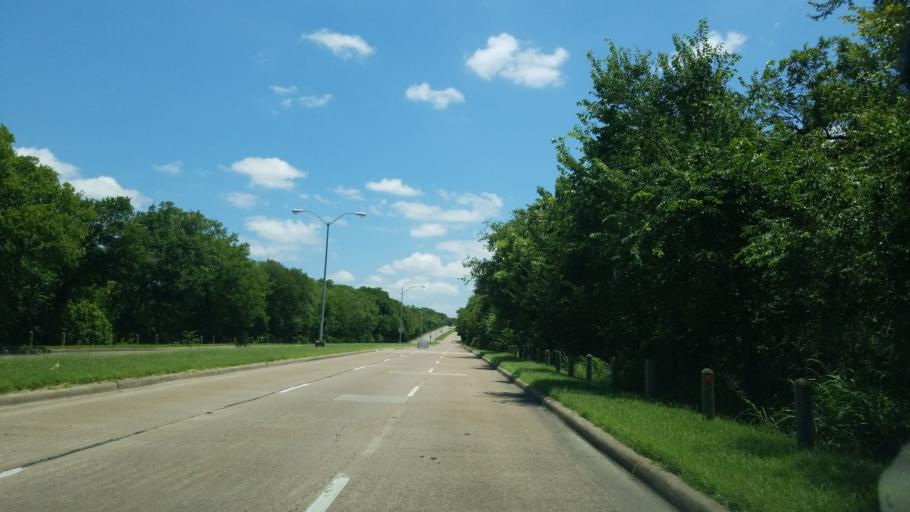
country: US
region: Texas
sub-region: Dallas County
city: Balch Springs
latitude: 32.7492
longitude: -96.7110
